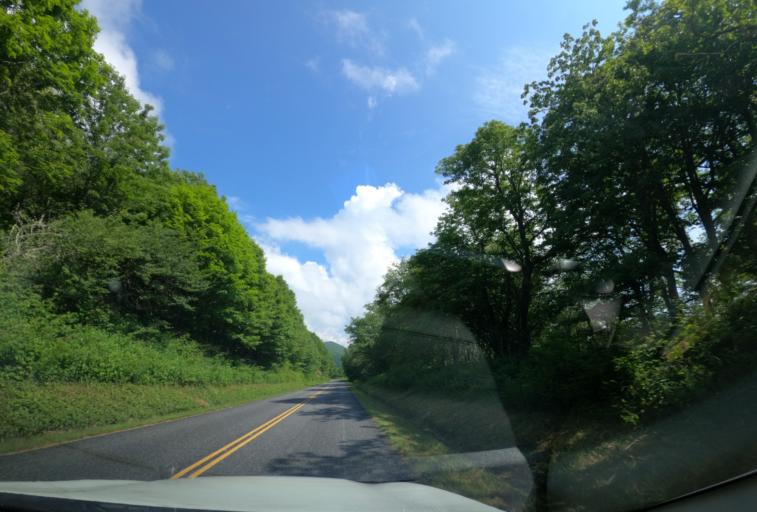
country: US
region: North Carolina
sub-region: Haywood County
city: Hazelwood
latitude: 35.3927
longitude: -83.0378
